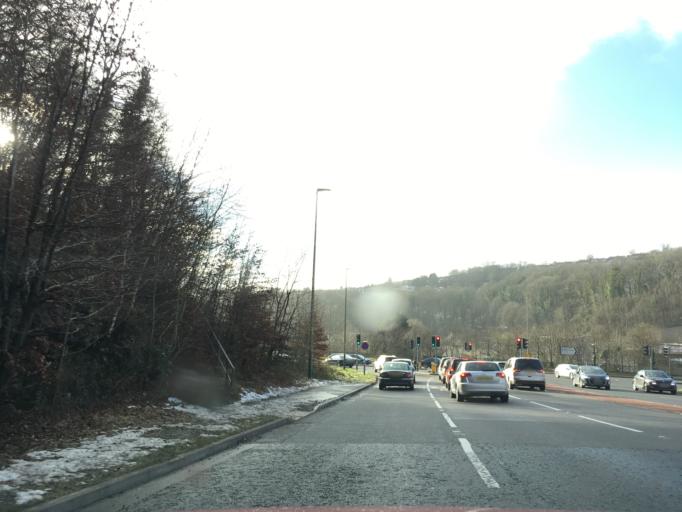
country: GB
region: Wales
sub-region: Caerphilly County Borough
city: Crumlin
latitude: 51.6790
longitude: -3.1372
